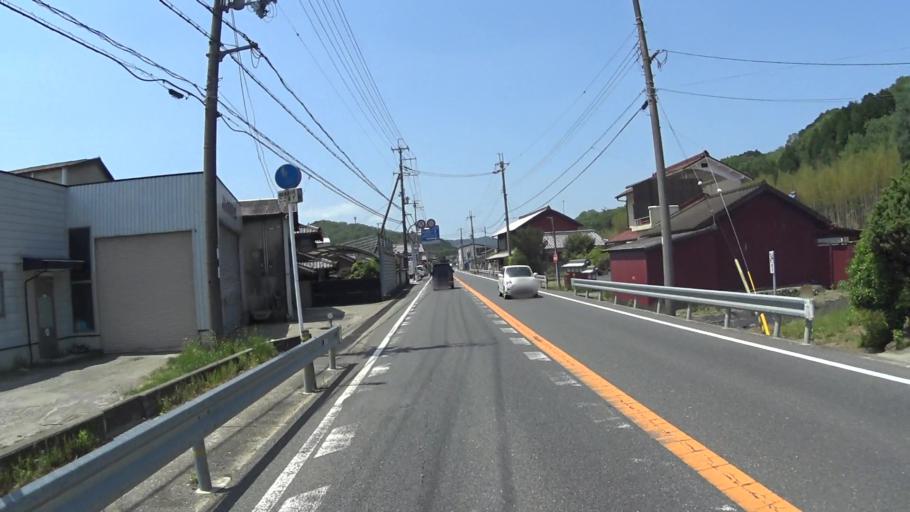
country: JP
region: Kyoto
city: Kameoka
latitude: 35.0917
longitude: 135.4931
